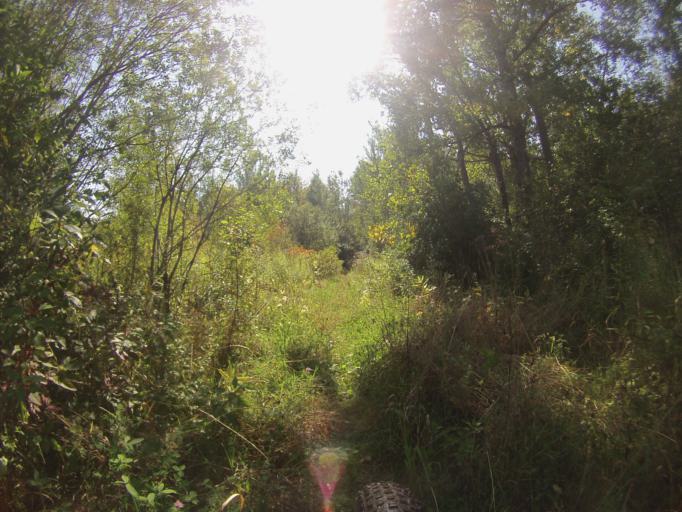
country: CA
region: Ontario
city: Ottawa
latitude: 45.3731
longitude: -75.6400
